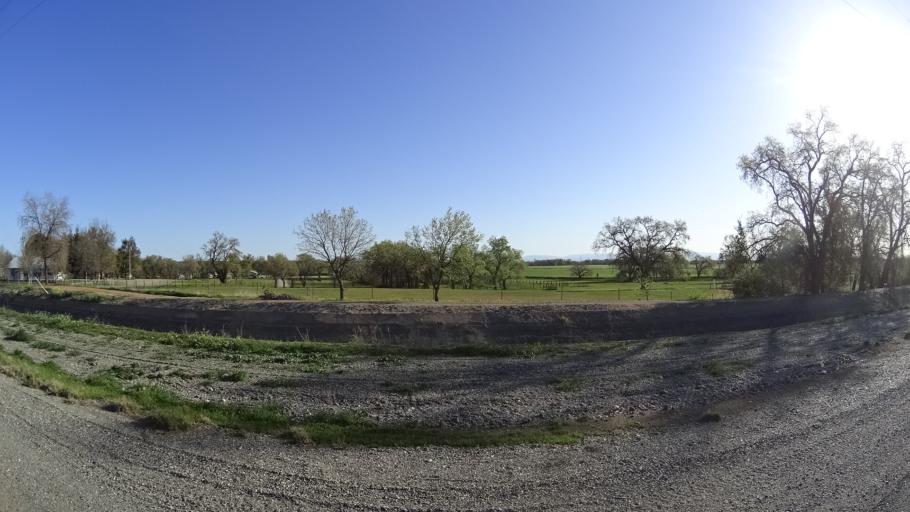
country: US
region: California
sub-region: Glenn County
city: Orland
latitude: 39.7871
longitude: -122.3024
